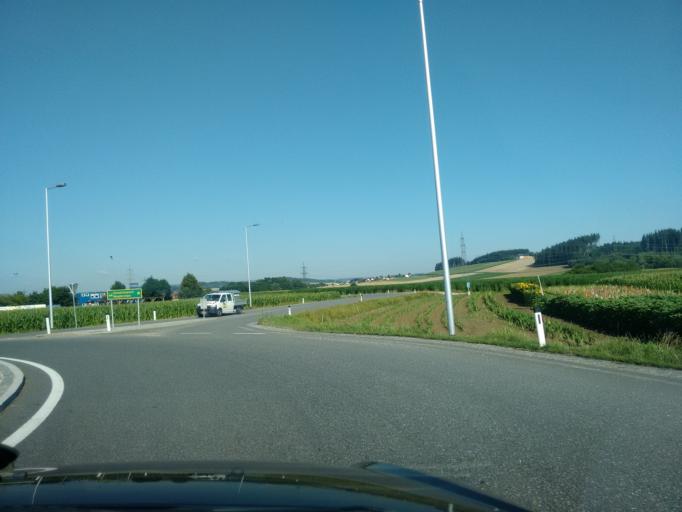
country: AT
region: Upper Austria
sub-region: Wels-Land
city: Stadl-Paura
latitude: 48.0912
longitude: 13.8520
